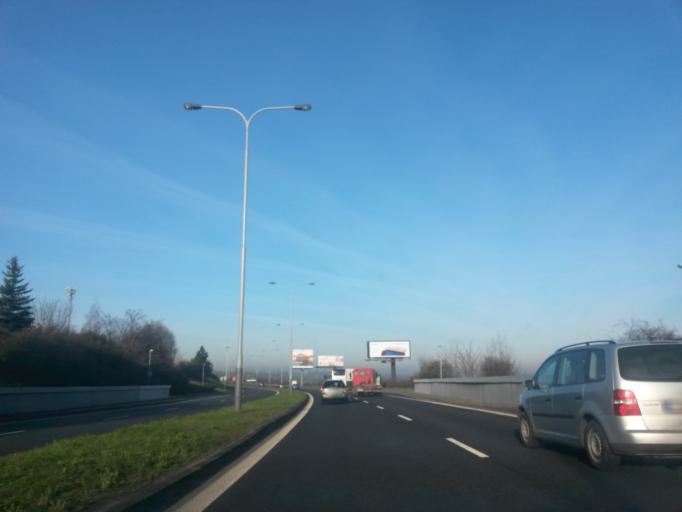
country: CZ
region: Praha
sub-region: Praha 12
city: Modrany
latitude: 50.0265
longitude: 14.3623
